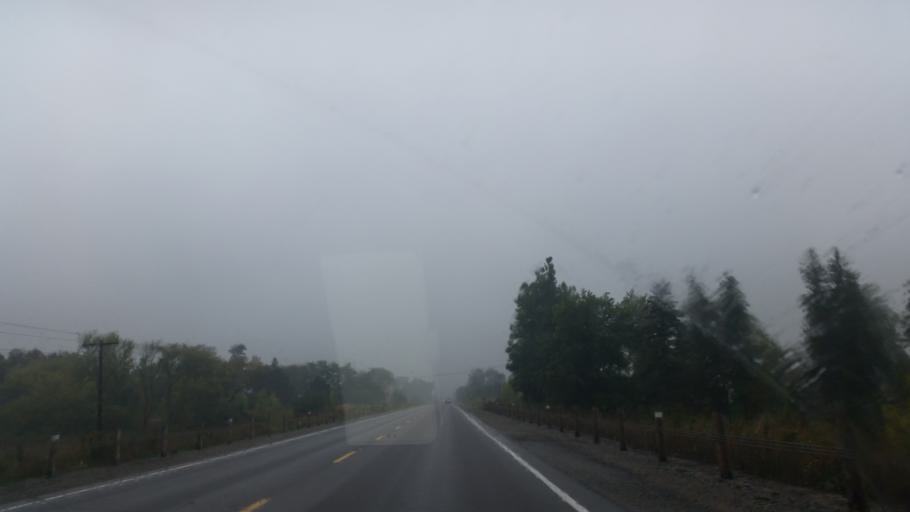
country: CA
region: Ontario
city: Stratford
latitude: 43.2885
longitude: -81.0525
